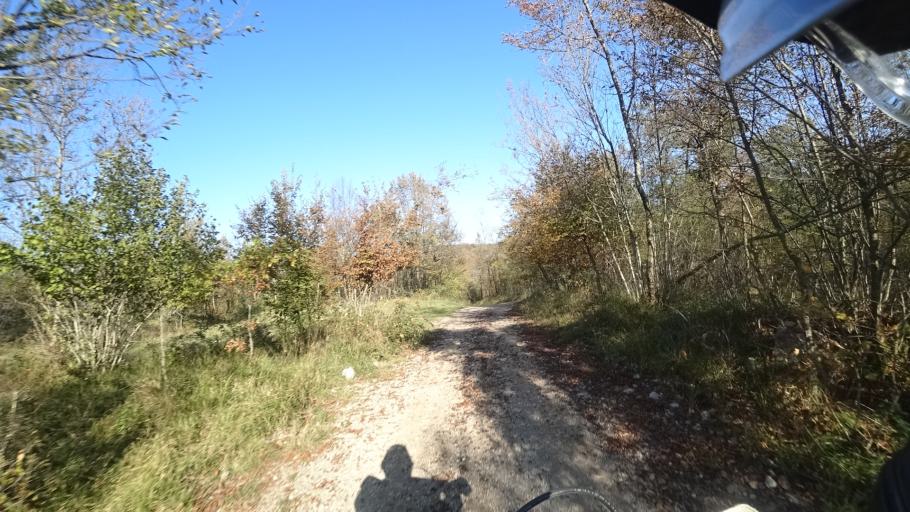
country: HR
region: Primorsko-Goranska
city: Klana
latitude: 45.4199
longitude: 14.3426
